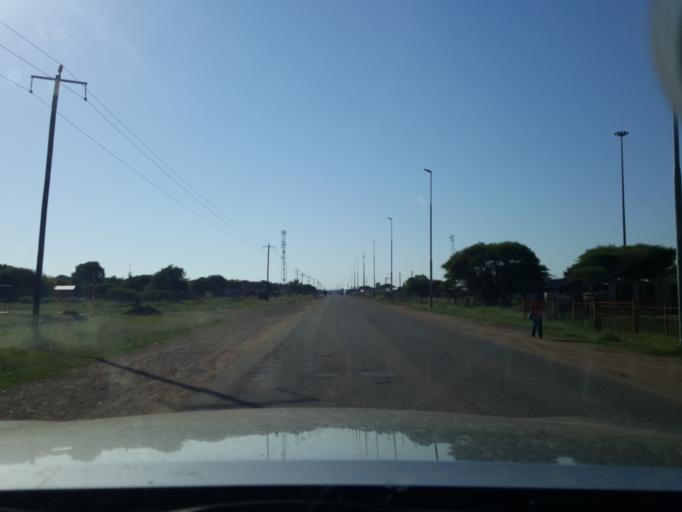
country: ZA
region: North-West
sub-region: Ngaka Modiri Molema District Municipality
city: Mmabatho
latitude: -25.8274
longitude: 25.6480
